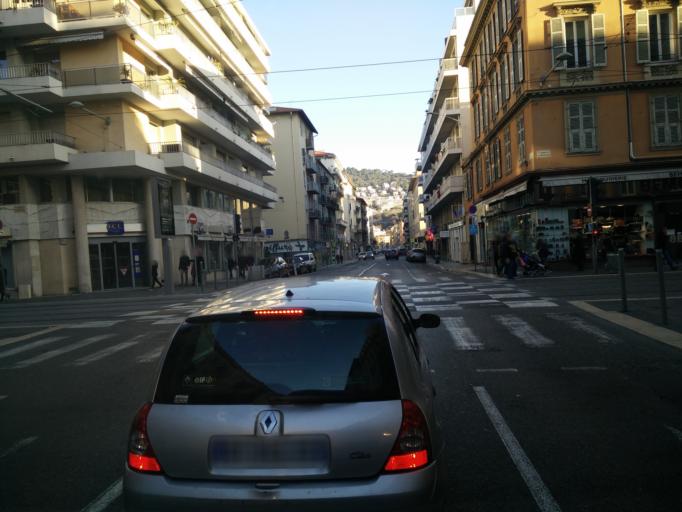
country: FR
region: Provence-Alpes-Cote d'Azur
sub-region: Departement des Alpes-Maritimes
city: Nice
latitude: 43.7024
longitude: 7.2808
